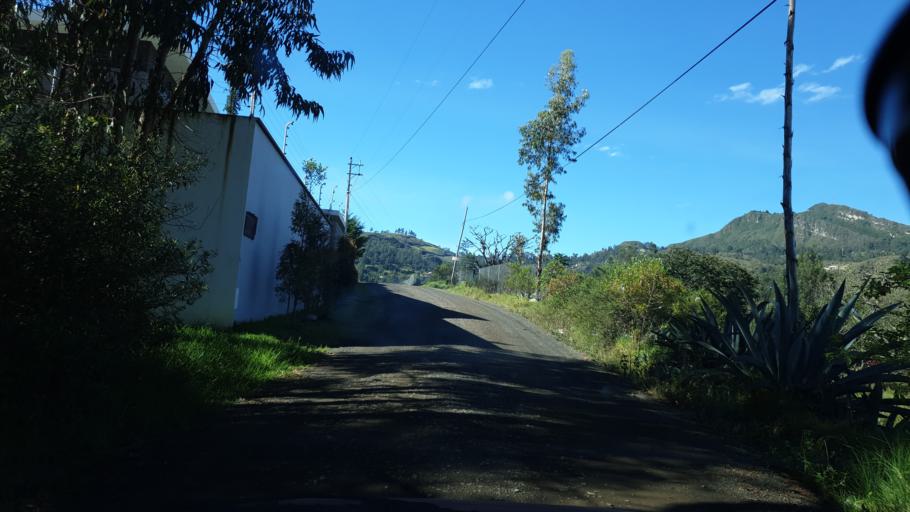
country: EC
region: Azuay
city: Llacao
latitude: -2.8656
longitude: -78.9121
